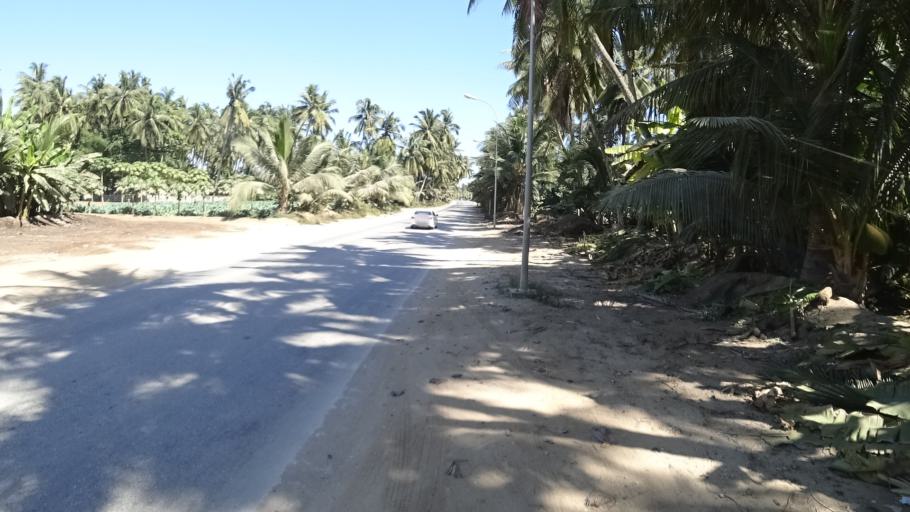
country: OM
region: Zufar
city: Salalah
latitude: 17.0117
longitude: 54.1114
